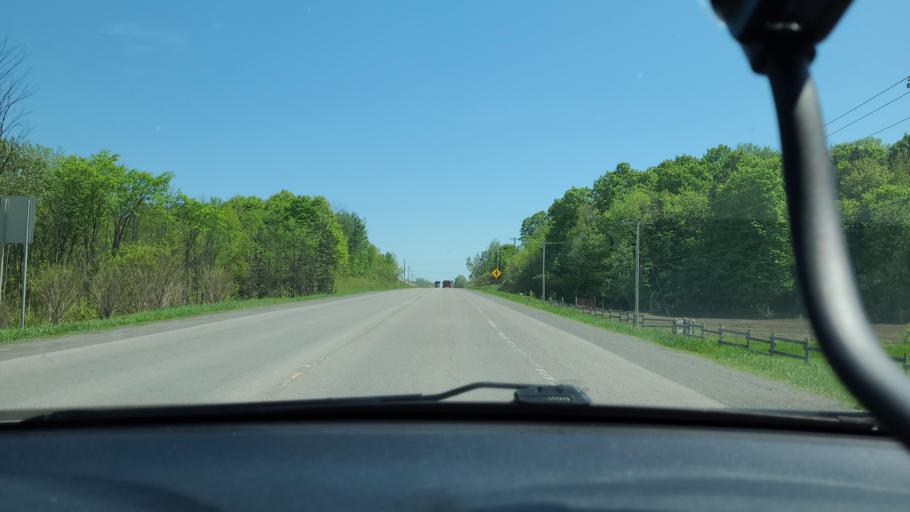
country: CA
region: Quebec
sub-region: Laurentides
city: Saint-Colomban
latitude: 45.6682
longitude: -74.1746
